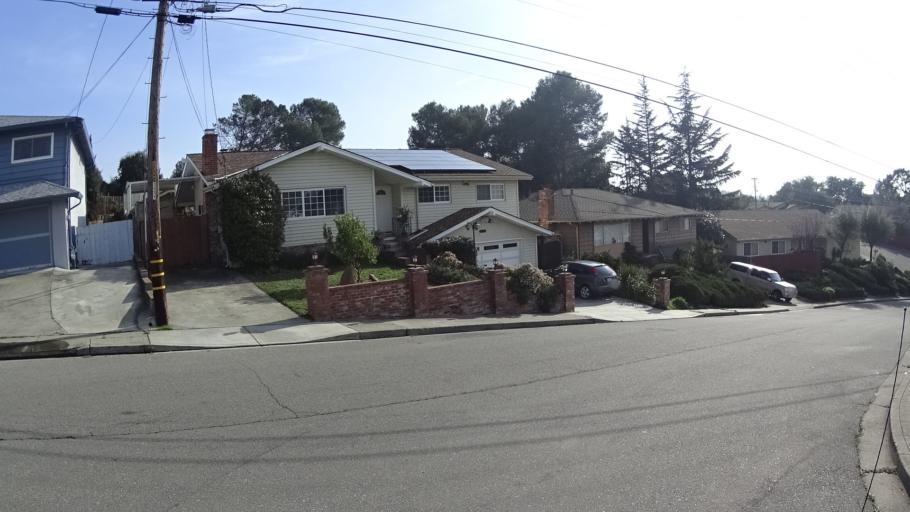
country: US
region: California
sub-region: Alameda County
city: Fairview
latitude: 37.6891
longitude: -122.0583
